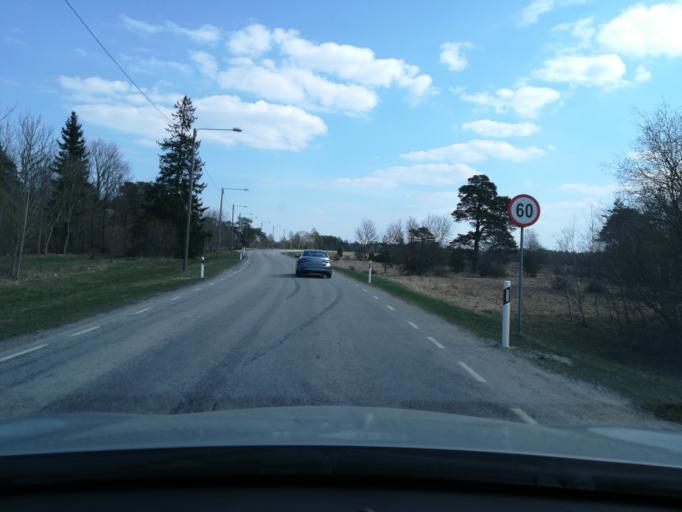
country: EE
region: Harju
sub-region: Keila linn
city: Keila
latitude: 59.3857
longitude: 24.4160
